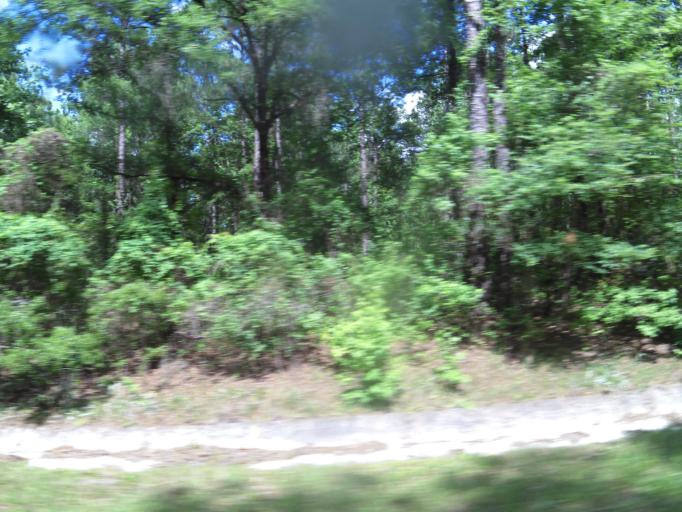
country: US
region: Florida
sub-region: Clay County
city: Asbury Lake
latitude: 29.8953
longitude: -81.8761
